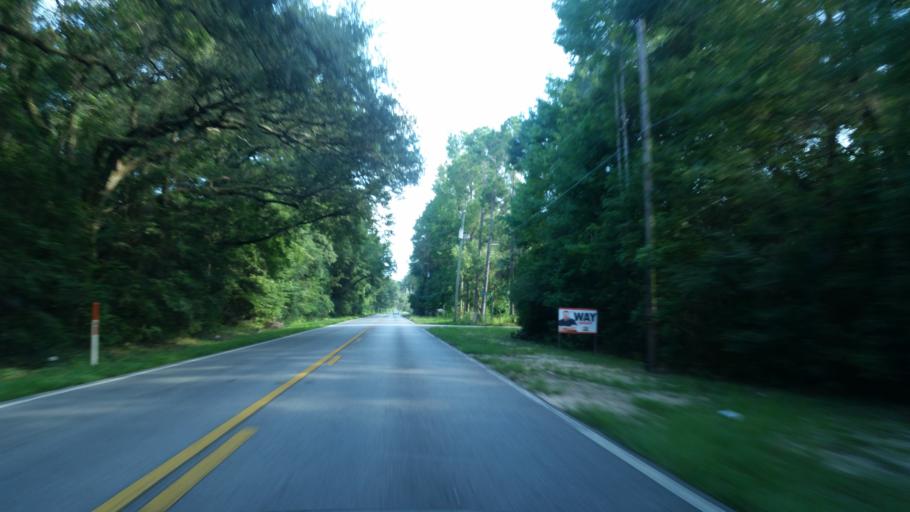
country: US
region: Florida
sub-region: Santa Rosa County
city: Bagdad
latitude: 30.5949
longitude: -87.0311
